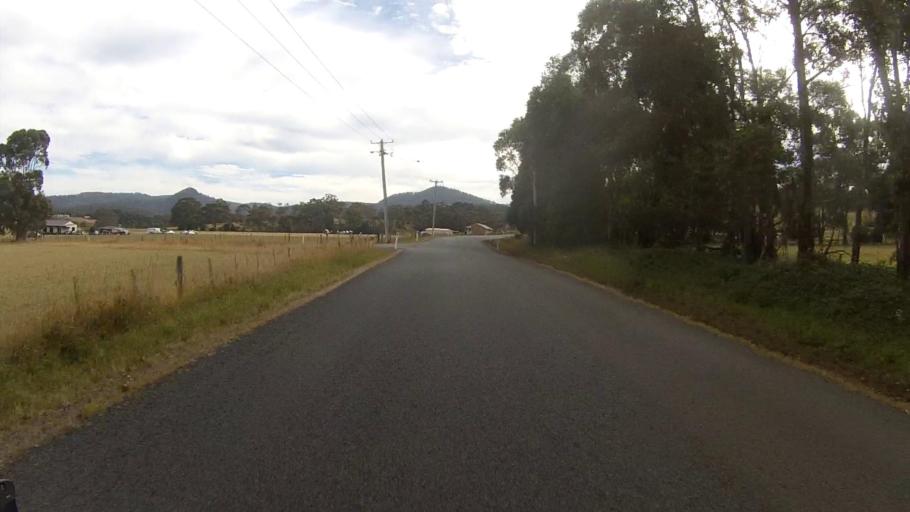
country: AU
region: Tasmania
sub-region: Sorell
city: Sorell
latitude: -42.7912
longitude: 147.7998
